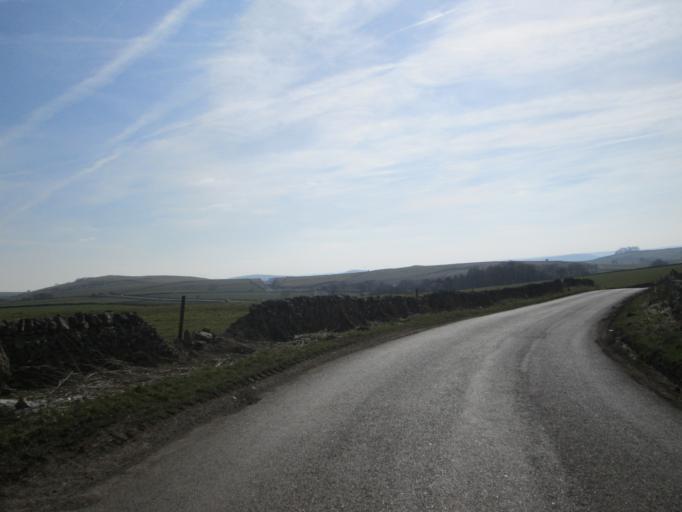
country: GB
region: England
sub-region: Derbyshire
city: Tideswell
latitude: 53.1739
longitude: -1.7776
